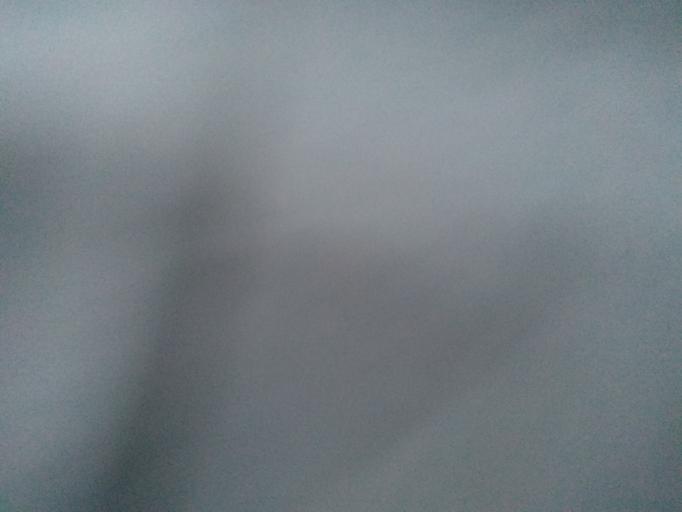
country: BD
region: Dhaka
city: Azimpur
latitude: 23.7772
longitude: 90.3805
